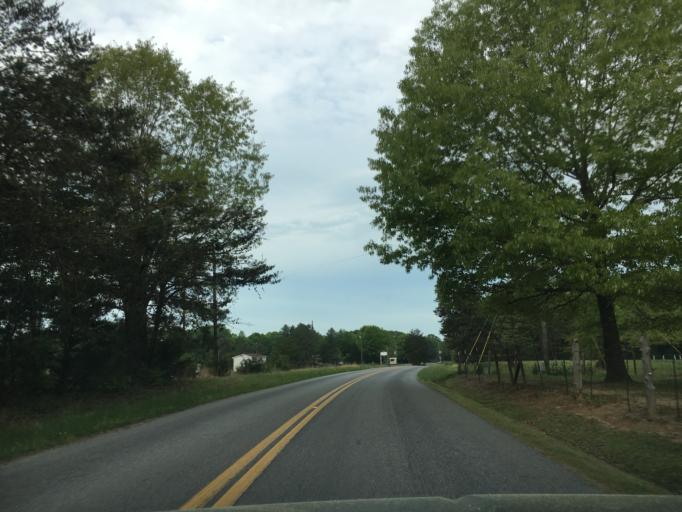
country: US
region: Virginia
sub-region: Halifax County
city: Halifax
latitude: 36.9080
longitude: -78.9218
